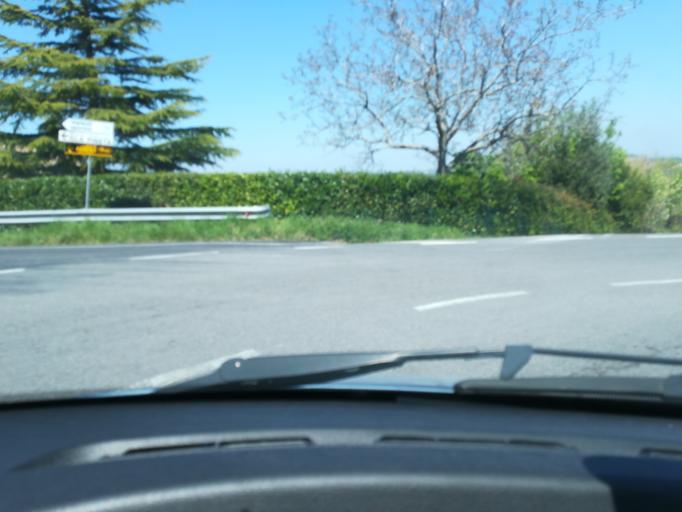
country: IT
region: The Marches
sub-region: Provincia di Macerata
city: Cingoli
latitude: 43.3891
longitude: 13.2025
